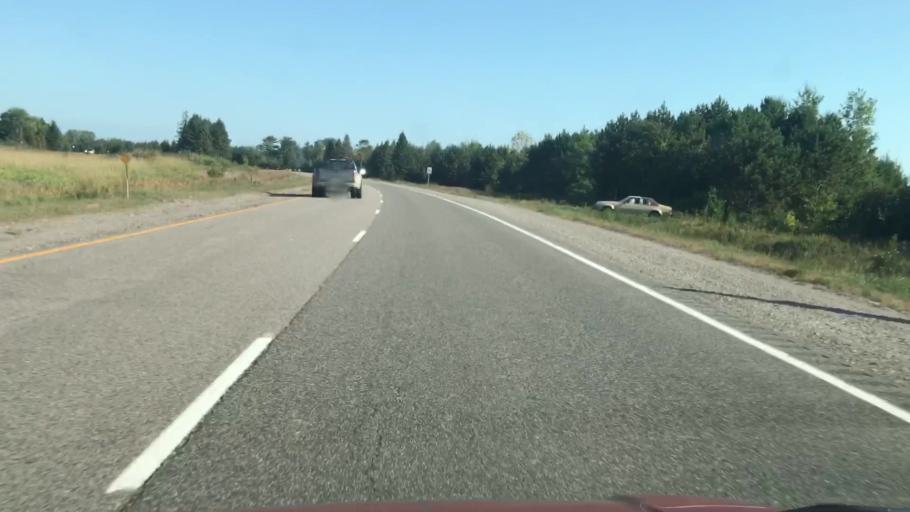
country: US
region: Michigan
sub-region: Chippewa County
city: Sault Ste. Marie
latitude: 46.3400
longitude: -84.0634
